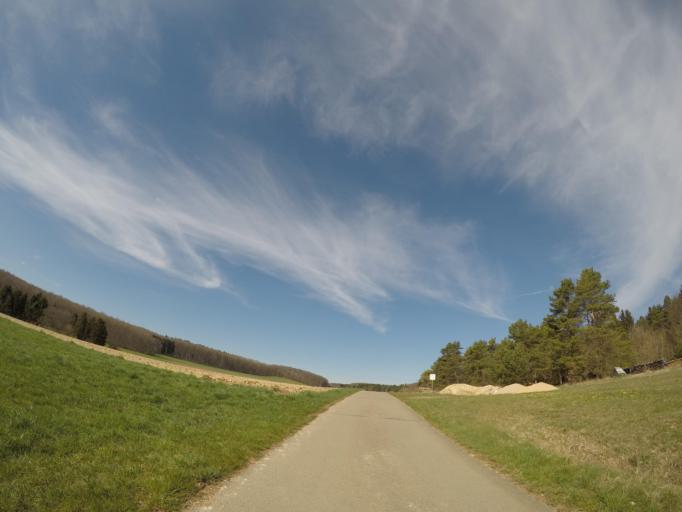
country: DE
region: Baden-Wuerttemberg
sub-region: Tuebingen Region
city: Mehrstetten
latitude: 48.3205
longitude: 9.5740
